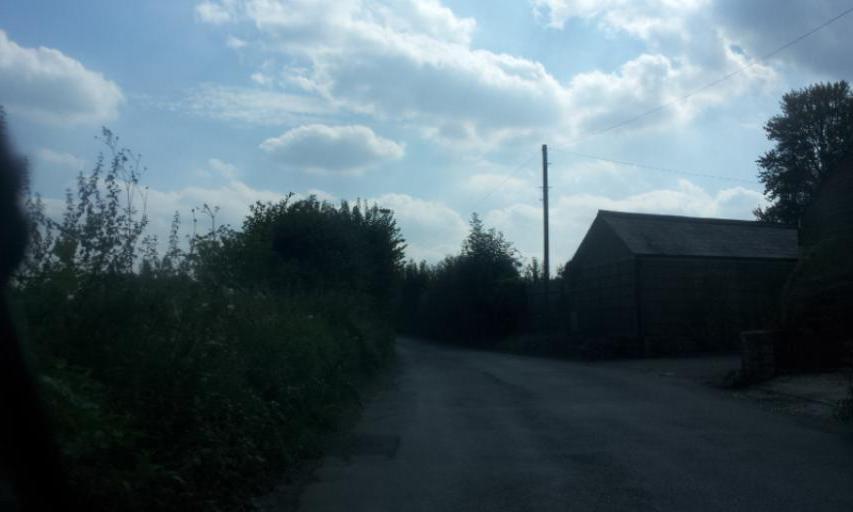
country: GB
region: England
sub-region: Kent
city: Maidstone
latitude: 51.2521
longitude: 0.5128
